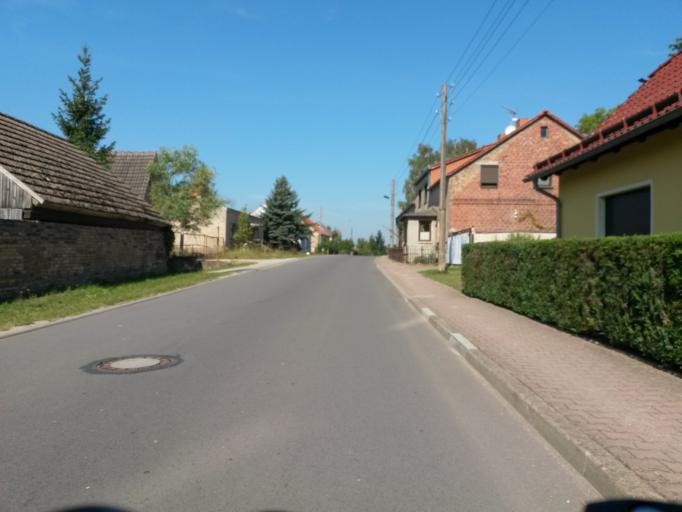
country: DE
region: Brandenburg
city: Templin
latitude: 53.0494
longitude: 13.4410
